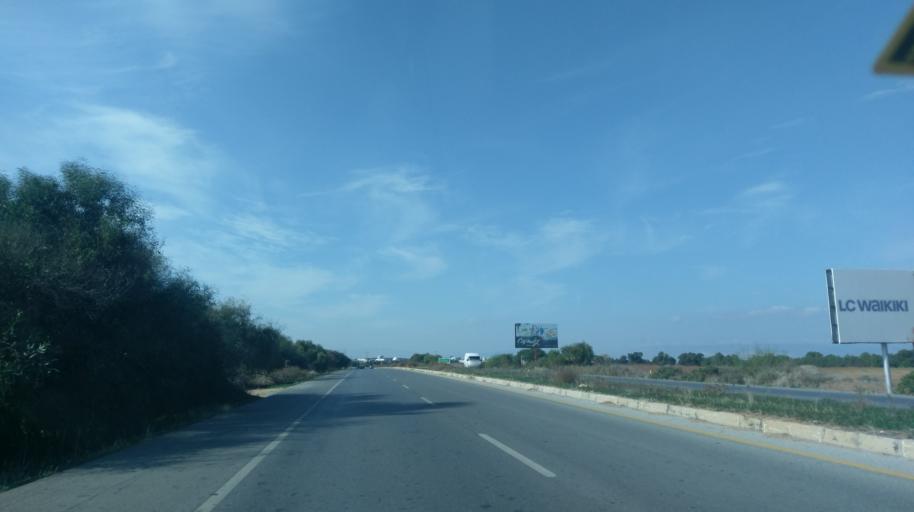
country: CY
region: Ammochostos
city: Famagusta
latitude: 35.1259
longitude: 33.9035
